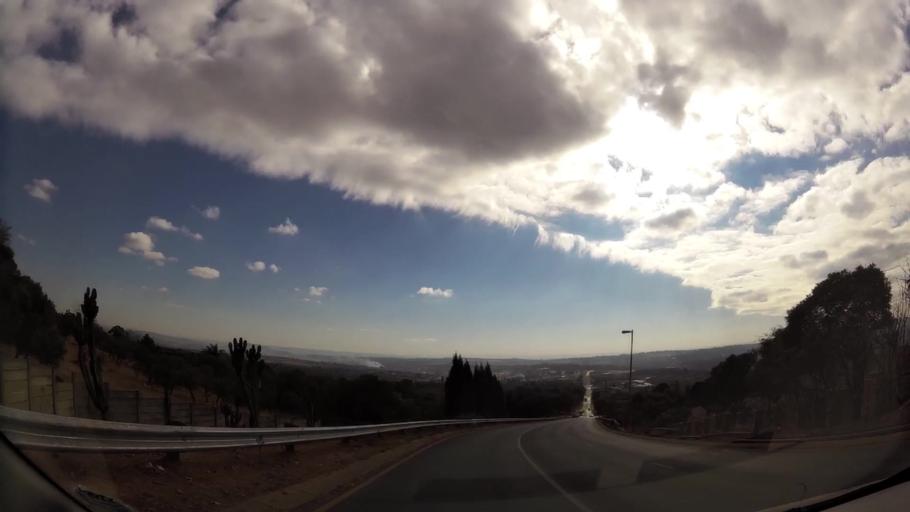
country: ZA
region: Gauteng
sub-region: City of Johannesburg Metropolitan Municipality
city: Roodepoort
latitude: -26.1012
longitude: 27.8638
